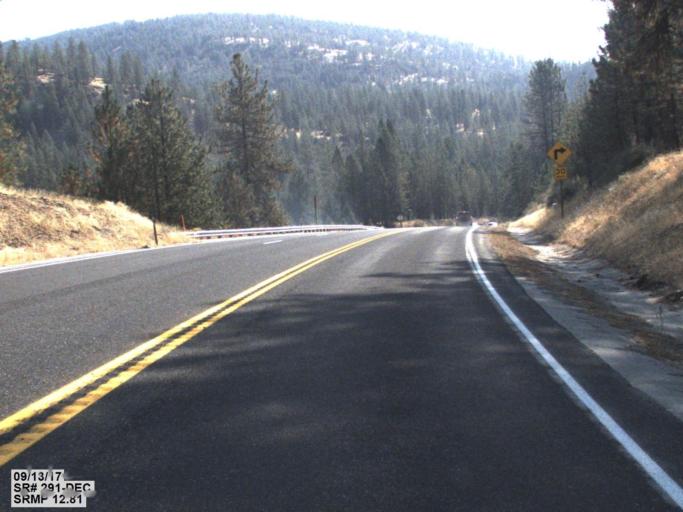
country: US
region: Washington
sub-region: Spokane County
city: Fairwood
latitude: 47.8112
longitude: -117.5578
